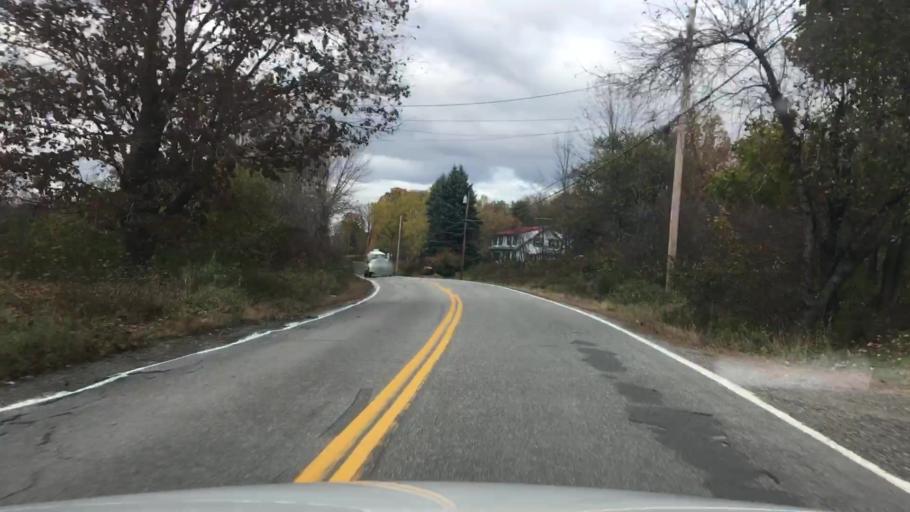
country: US
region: Maine
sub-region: Androscoggin County
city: Sabattus
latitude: 44.1504
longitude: -70.0822
